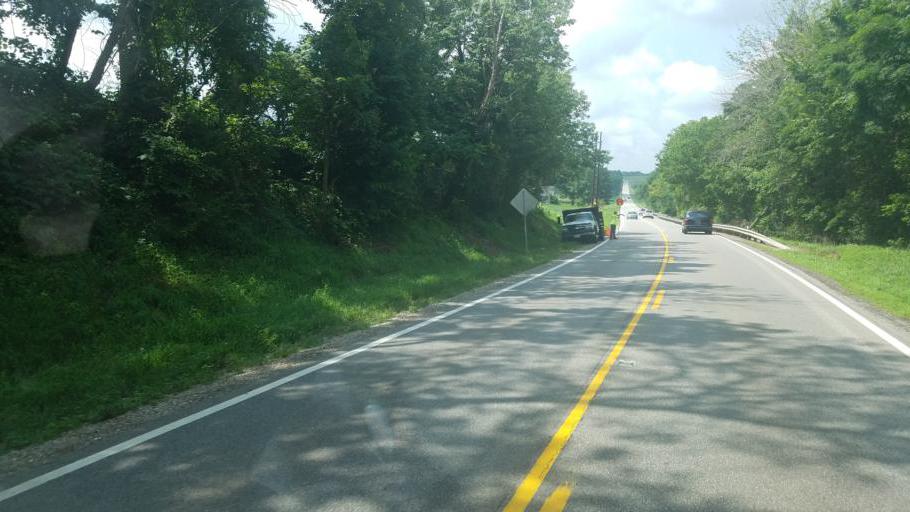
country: US
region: Ohio
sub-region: Fairfield County
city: Lancaster
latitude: 39.6644
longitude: -82.7078
